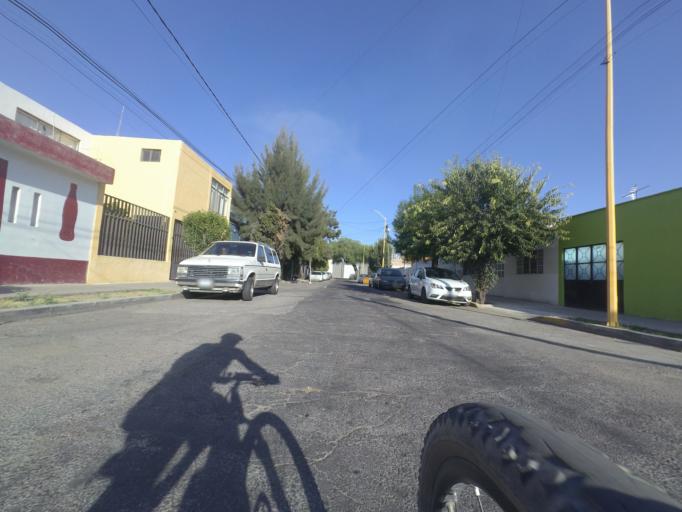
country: MX
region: Aguascalientes
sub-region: Aguascalientes
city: Aguascalientes
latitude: 21.8687
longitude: -102.2965
